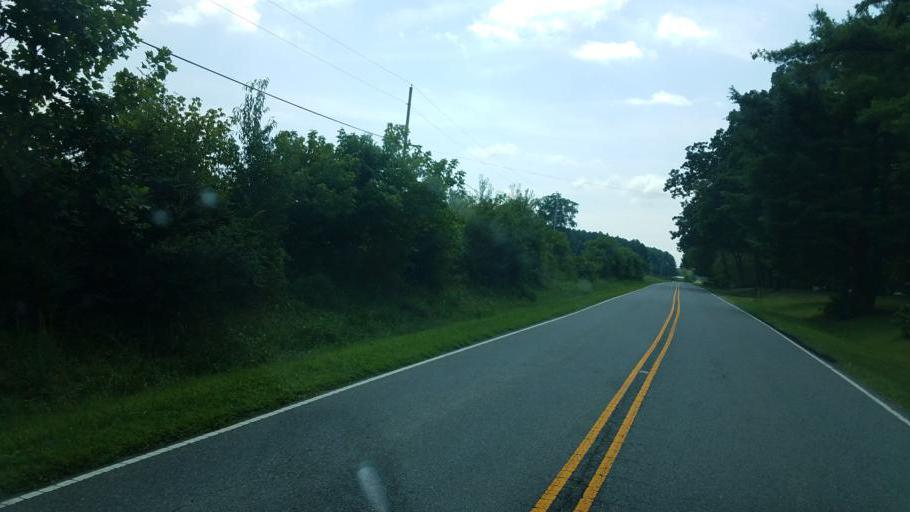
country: US
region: North Carolina
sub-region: Gaston County
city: Cherryville
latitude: 35.4154
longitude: -81.4080
